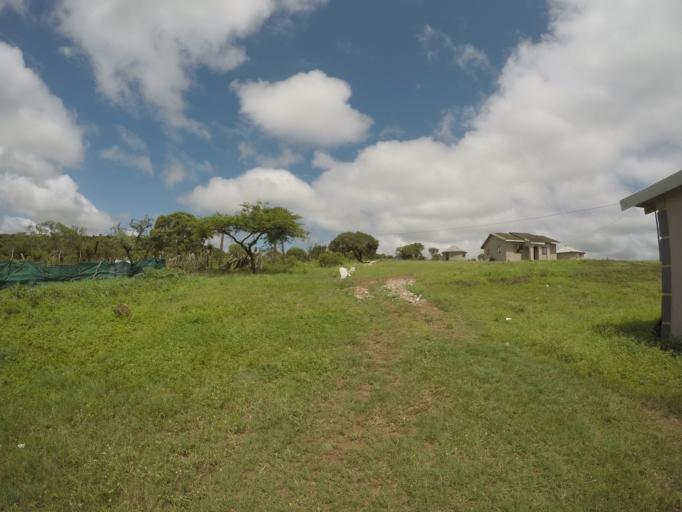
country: ZA
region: KwaZulu-Natal
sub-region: uThungulu District Municipality
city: Empangeni
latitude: -28.5736
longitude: 31.8289
